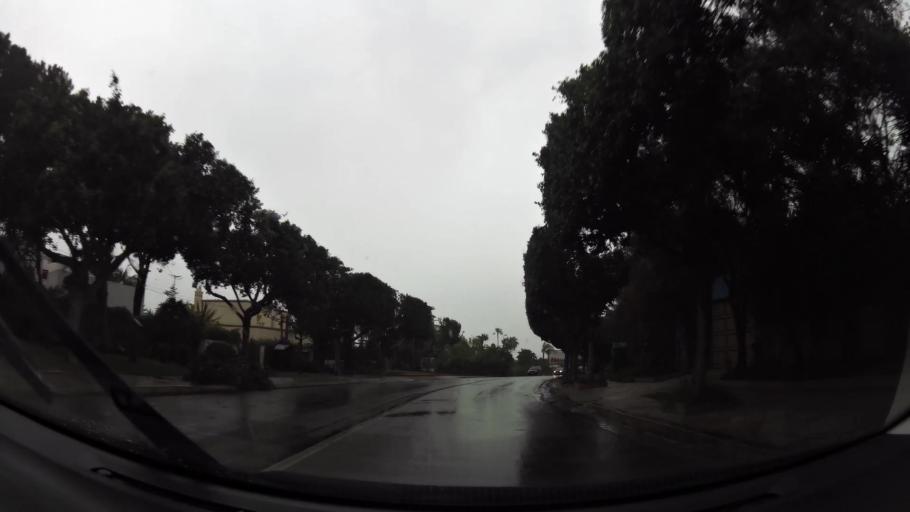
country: MA
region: Grand Casablanca
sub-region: Casablanca
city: Casablanca
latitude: 33.5861
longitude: -7.6676
